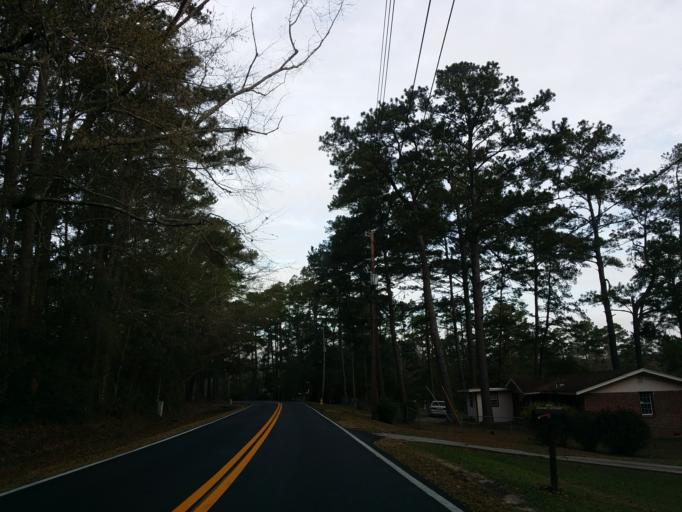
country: US
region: Florida
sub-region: Leon County
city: Tallahassee
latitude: 30.4720
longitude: -84.2156
